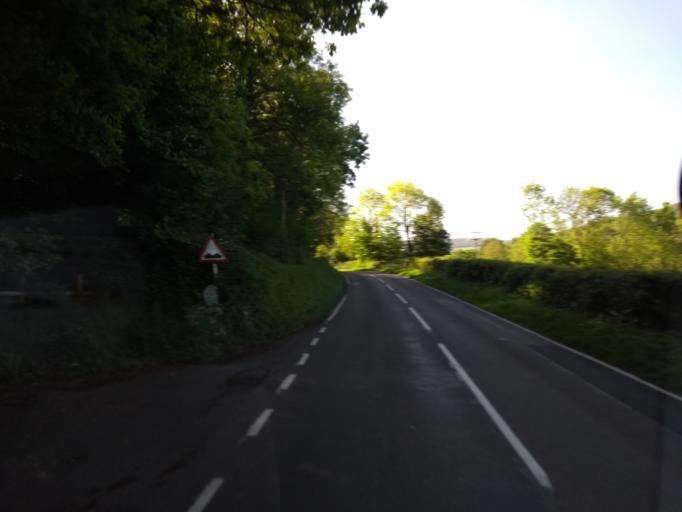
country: GB
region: England
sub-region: Somerset
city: Taunton
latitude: 50.9623
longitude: -3.0916
